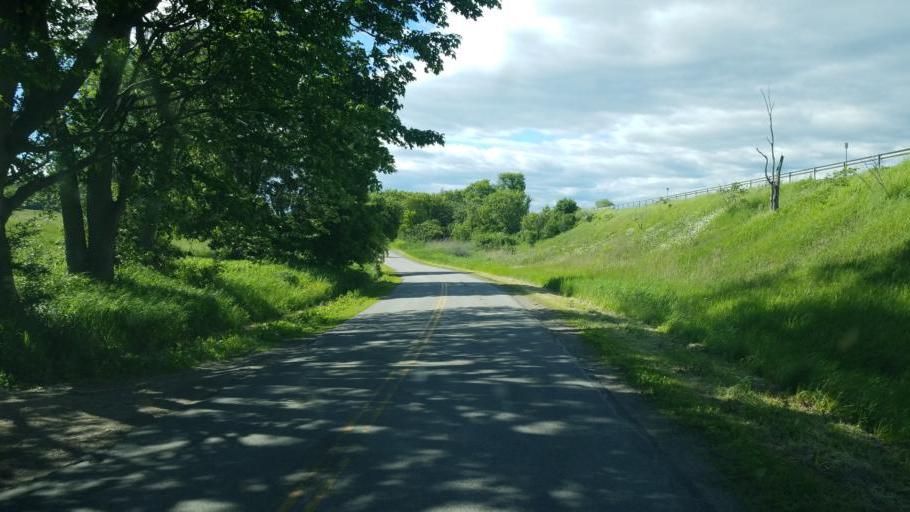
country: US
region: New York
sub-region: Montgomery County
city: Fort Plain
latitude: 42.9567
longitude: -74.6352
